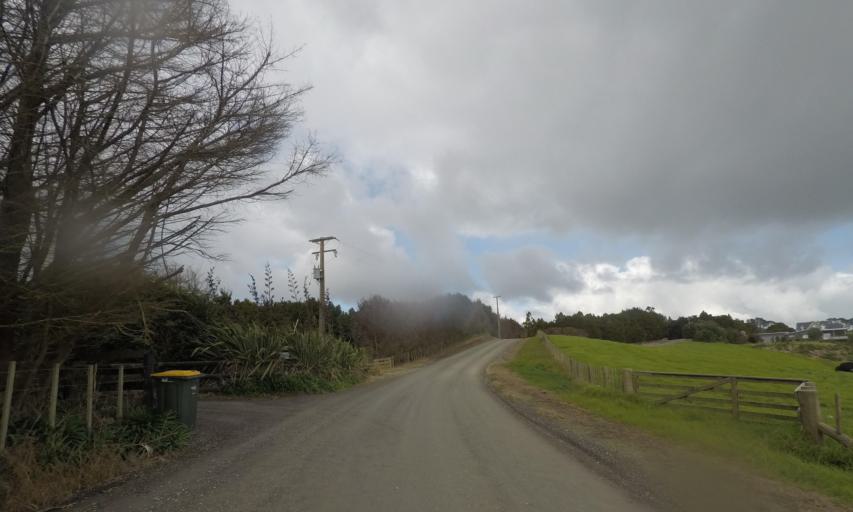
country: NZ
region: Auckland
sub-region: Auckland
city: Wellsford
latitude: -36.1675
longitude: 174.6028
